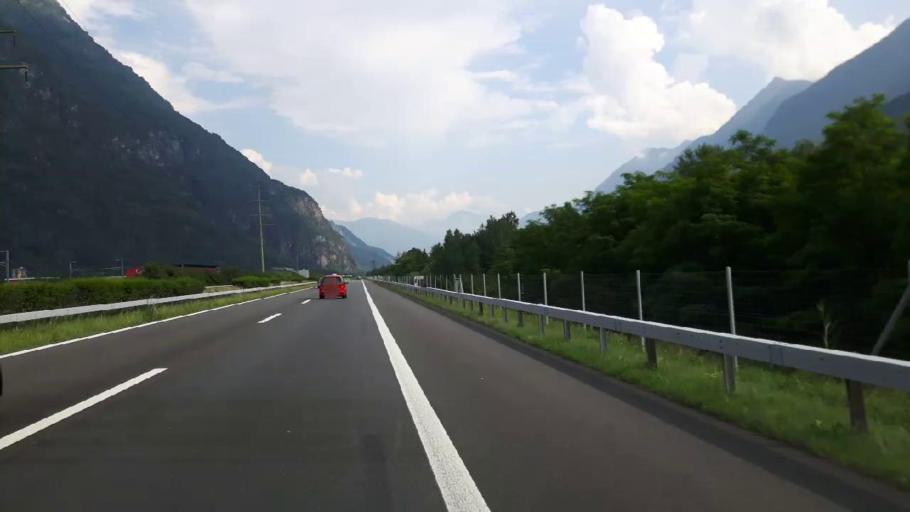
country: CH
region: Ticino
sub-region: Riviera District
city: Biasca
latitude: 46.3420
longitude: 8.9688
